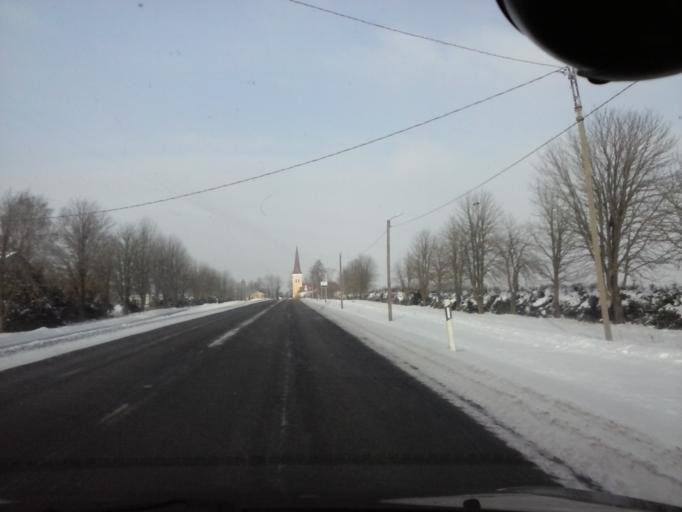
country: EE
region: Viljandimaa
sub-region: Abja vald
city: Abja-Paluoja
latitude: 58.3214
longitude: 25.3043
